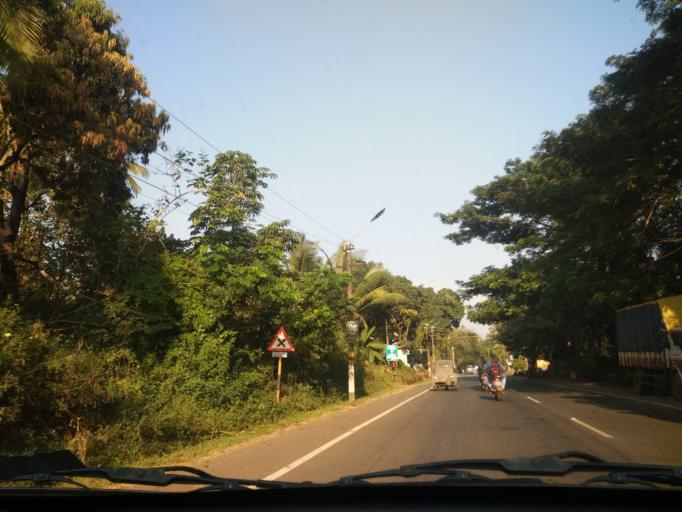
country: IN
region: Goa
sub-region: South Goa
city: Chinchinim
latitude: 15.2143
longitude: 73.9852
